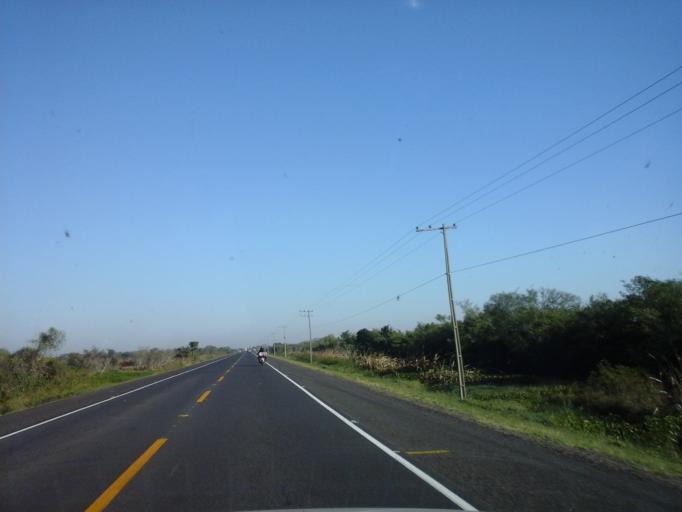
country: PY
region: Neembucu
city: Pilar
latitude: -26.8576
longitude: -58.1861
